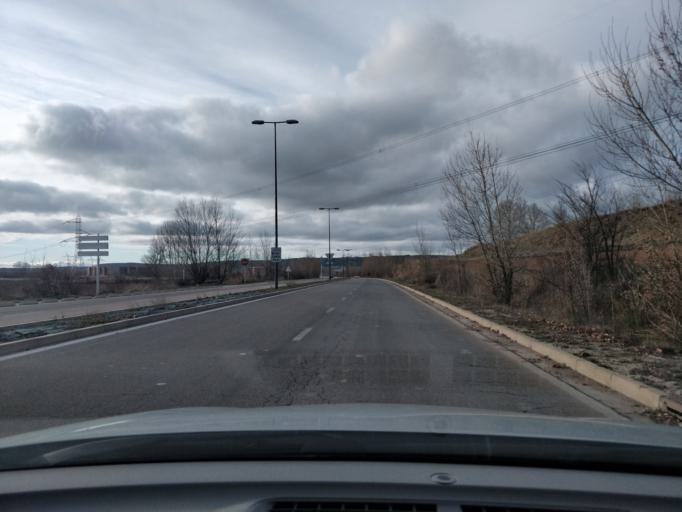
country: ES
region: Castille and Leon
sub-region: Provincia de Burgos
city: Villalbilla de Burgos
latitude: 42.3530
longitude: -3.7453
